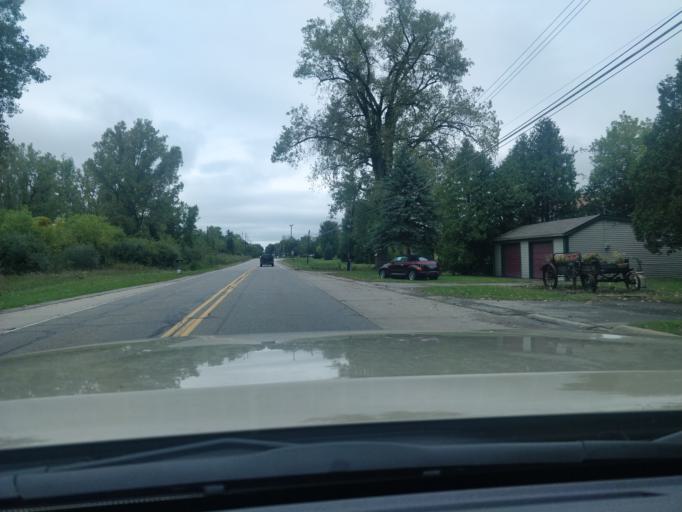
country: US
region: Michigan
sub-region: Wayne County
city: Romulus
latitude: 42.1760
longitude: -83.4033
